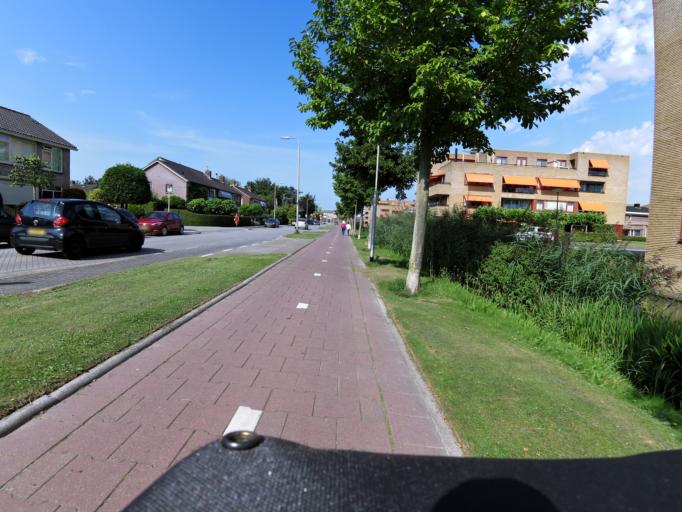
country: NL
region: South Holland
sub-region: Gemeente Oud-Beijerland
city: Oud-Beijerland
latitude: 51.8216
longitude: 4.4224
